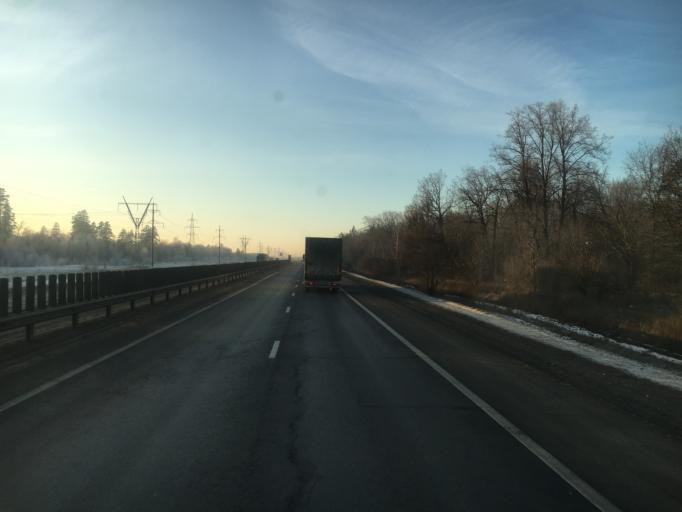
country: RU
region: Samara
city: Pribrezhnyy
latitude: 53.5164
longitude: 49.8584
